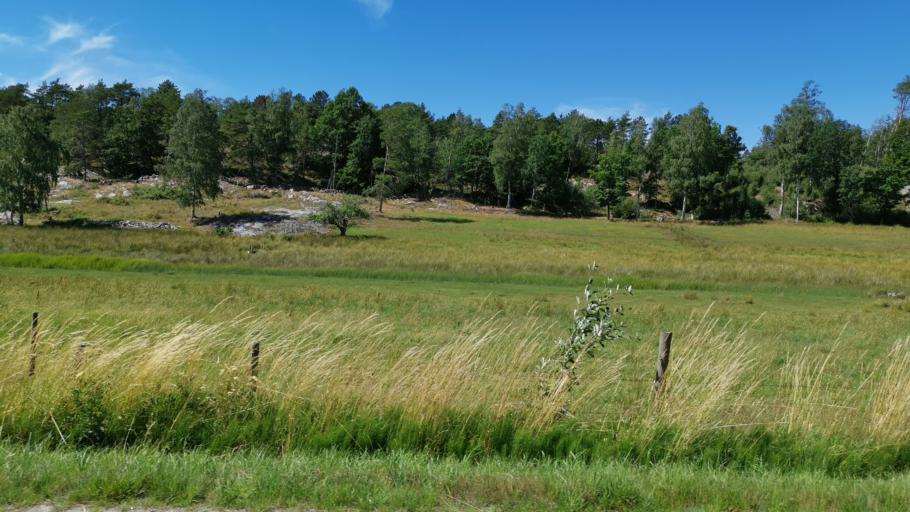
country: SE
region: Vaestra Goetaland
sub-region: Lysekils Kommun
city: Lysekil
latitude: 58.2209
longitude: 11.4560
